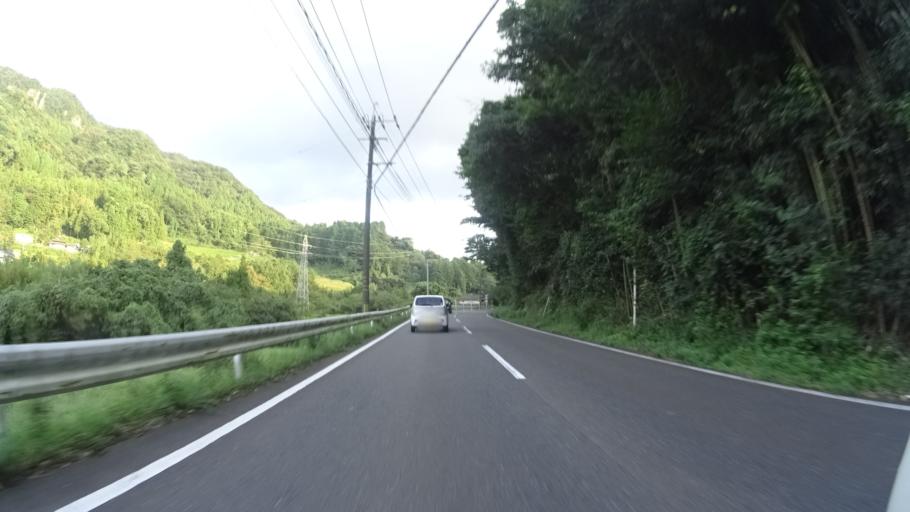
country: JP
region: Oita
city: Beppu
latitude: 33.3614
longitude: 131.3960
